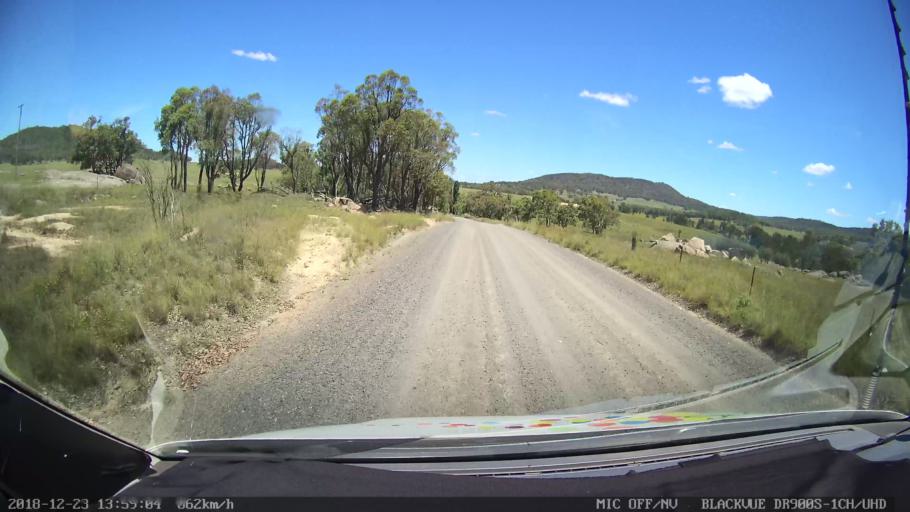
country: AU
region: New South Wales
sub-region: Tamworth Municipality
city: Manilla
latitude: -30.6044
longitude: 151.0949
